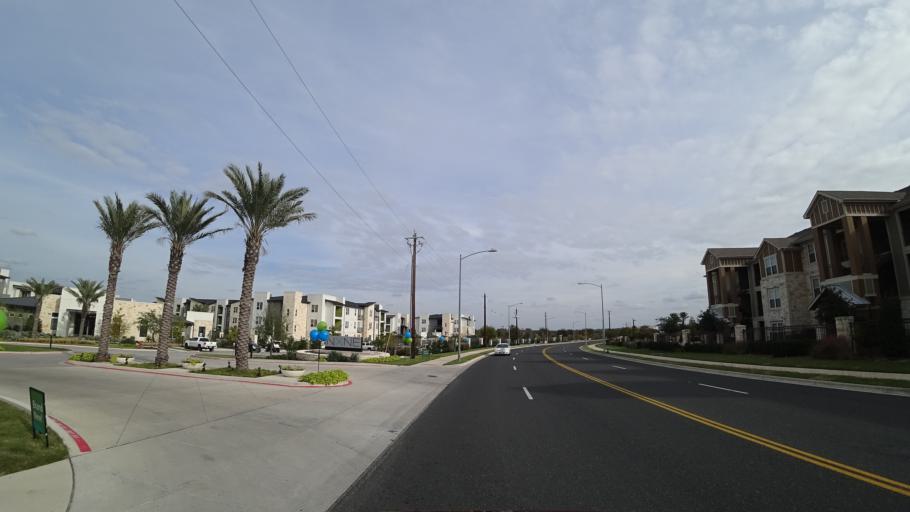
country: US
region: Texas
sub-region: Travis County
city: Wells Branch
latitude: 30.4297
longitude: -97.6664
